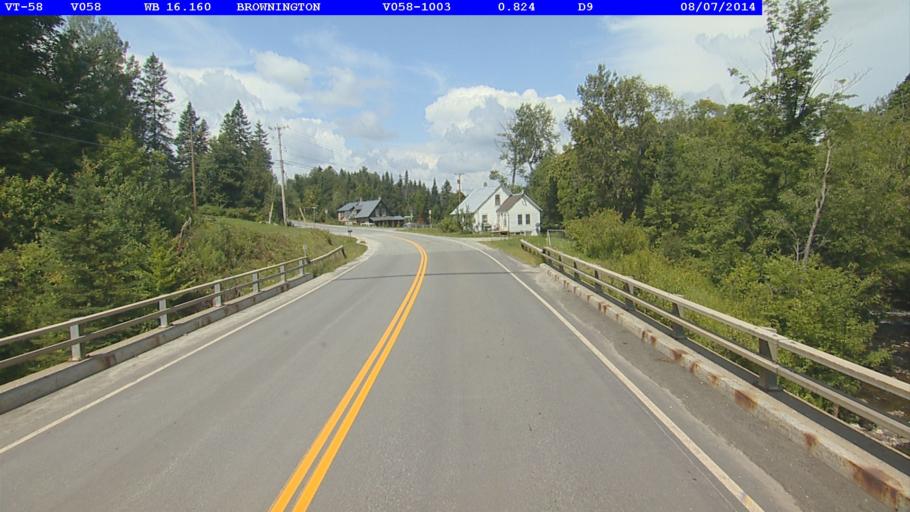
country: US
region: Vermont
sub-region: Orleans County
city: Newport
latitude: 44.8023
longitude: -72.1294
